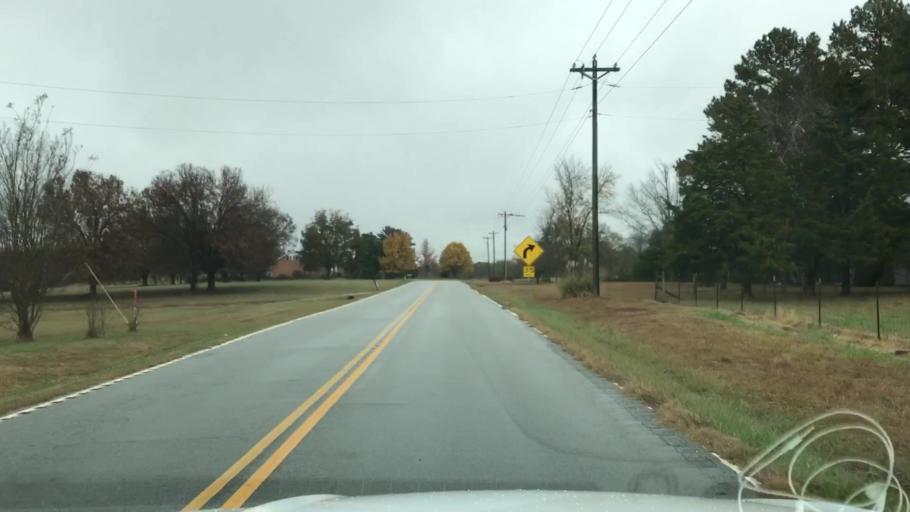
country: US
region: South Carolina
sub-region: Spartanburg County
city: Roebuck
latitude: 34.7857
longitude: -81.9167
